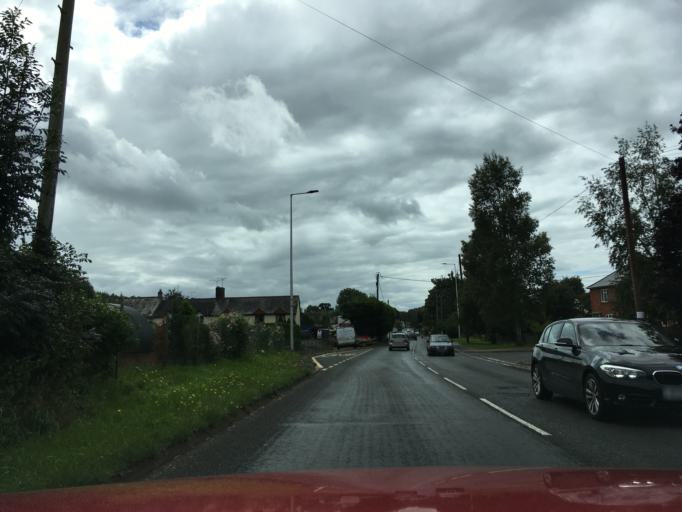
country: GB
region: England
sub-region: Devon
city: Cullompton
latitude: 50.8915
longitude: -3.3689
